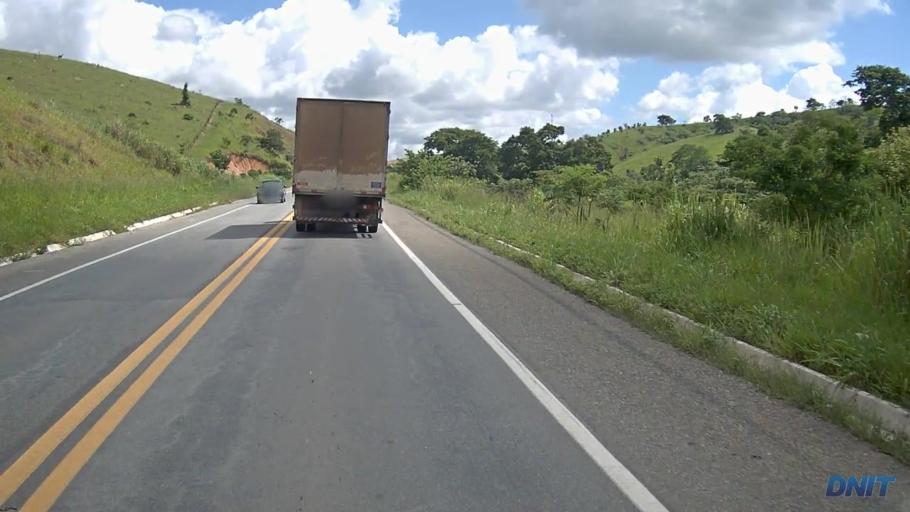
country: BR
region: Minas Gerais
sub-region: Governador Valadares
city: Governador Valadares
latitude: -19.0353
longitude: -42.1483
